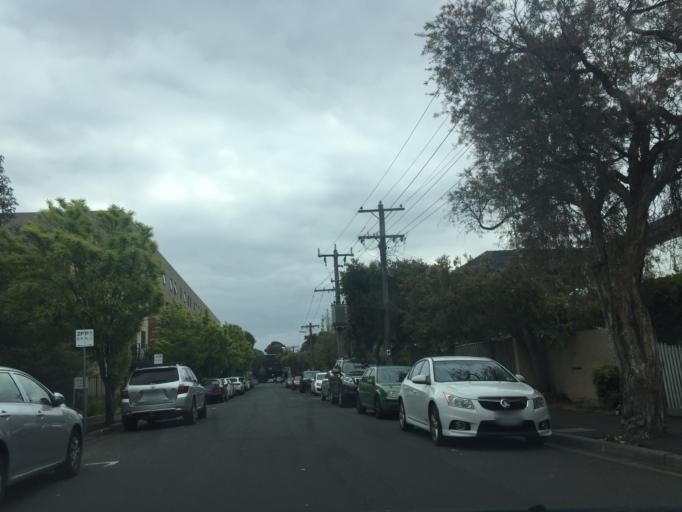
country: AU
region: Victoria
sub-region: Boroondara
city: Hawthorn East
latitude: -37.8200
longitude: 145.0382
